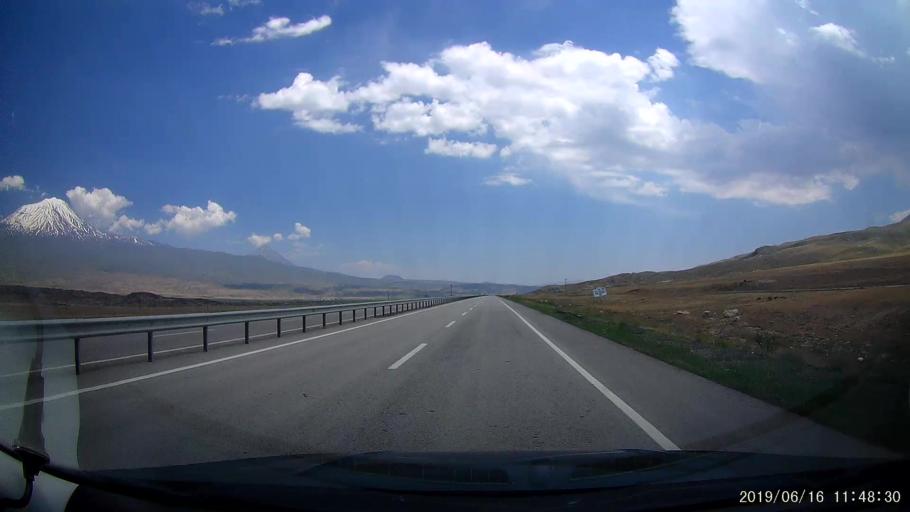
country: TR
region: Agri
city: Dogubayazit
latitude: 39.5580
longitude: 44.1448
